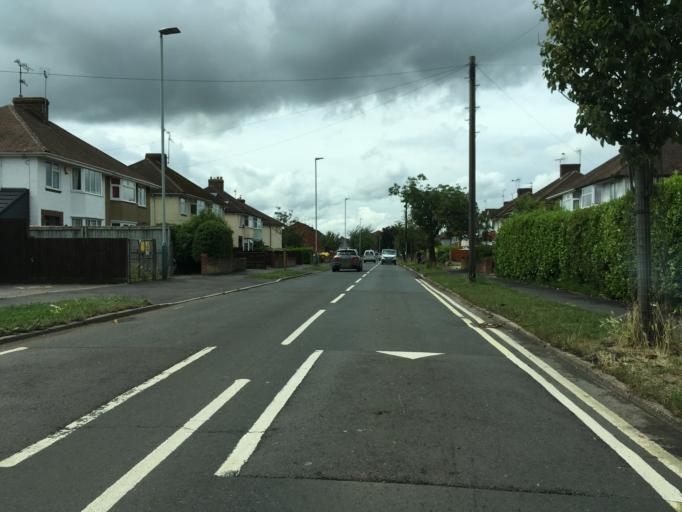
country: GB
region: England
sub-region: Gloucestershire
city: Swindon
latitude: 51.9074
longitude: -2.1051
